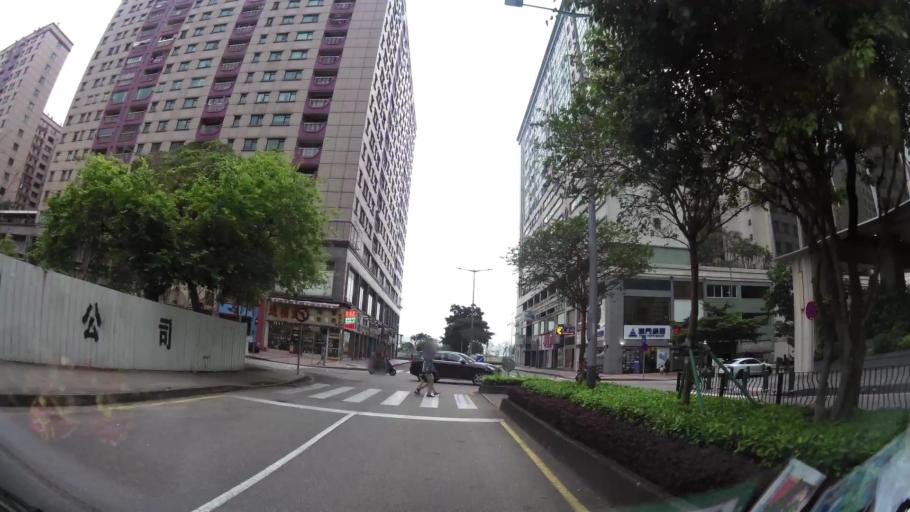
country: MO
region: Macau
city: Macau
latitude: 22.1872
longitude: 113.5499
